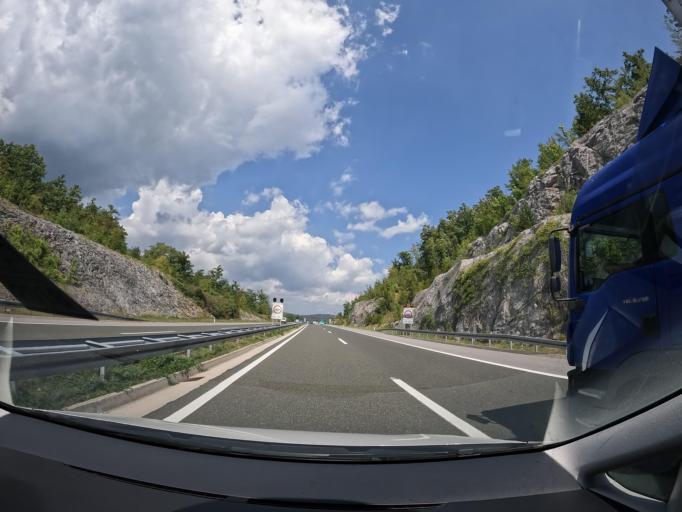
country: HR
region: Primorsko-Goranska
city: Matulji
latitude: 45.4509
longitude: 14.2711
